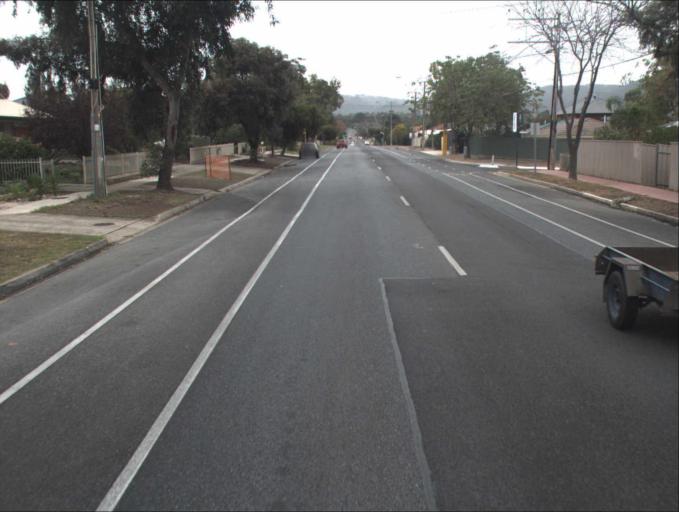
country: AU
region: South Australia
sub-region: Campbelltown
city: Paradise
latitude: -34.8574
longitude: 138.6664
